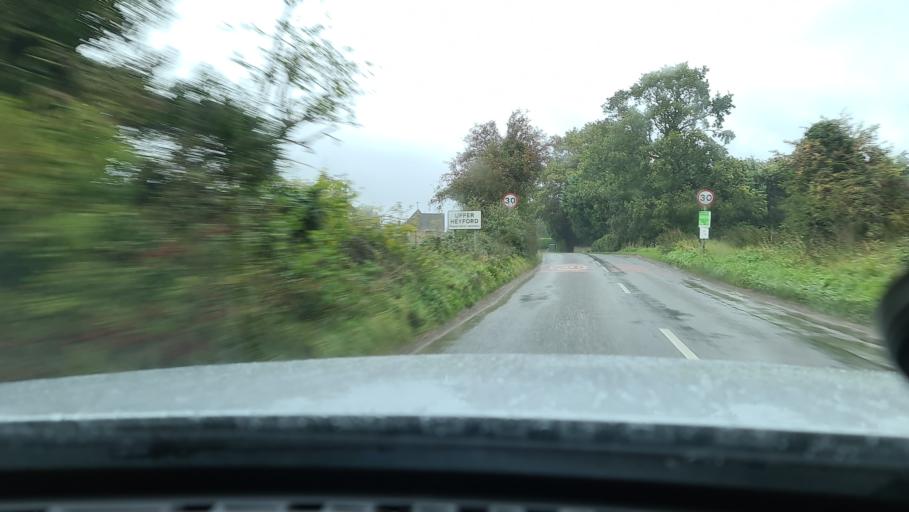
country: GB
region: England
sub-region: Oxfordshire
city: Somerton
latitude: 51.9285
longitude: -1.2764
